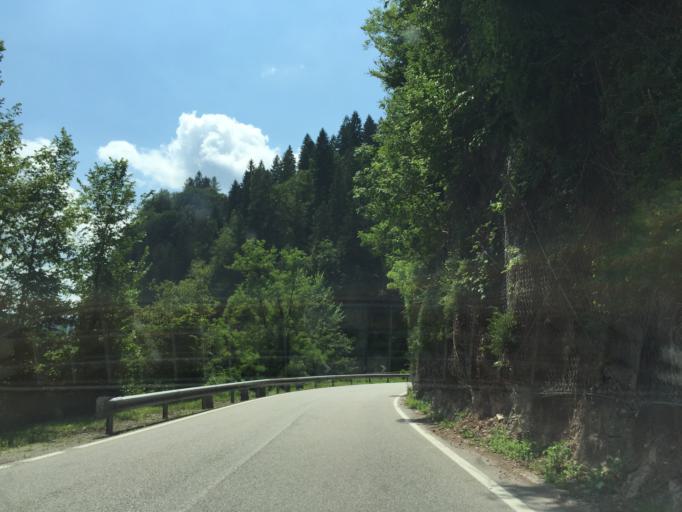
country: IT
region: Veneto
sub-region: Provincia di Belluno
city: Lamon
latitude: 46.0555
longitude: 11.7630
